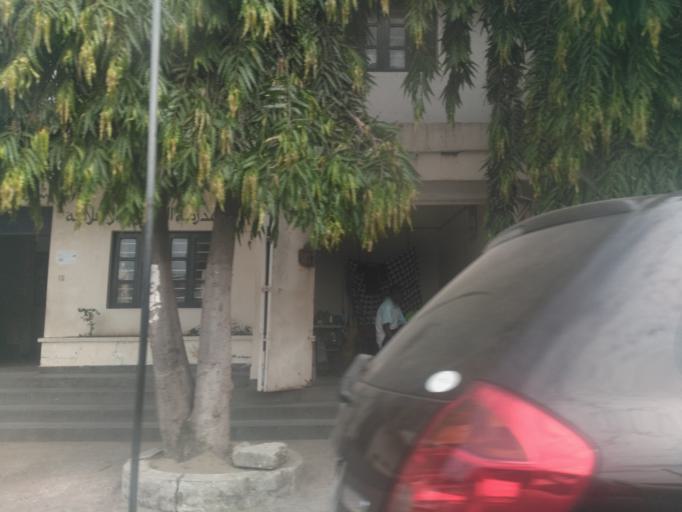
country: TZ
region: Zanzibar Urban/West
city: Zanzibar
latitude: -6.1694
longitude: 39.2040
